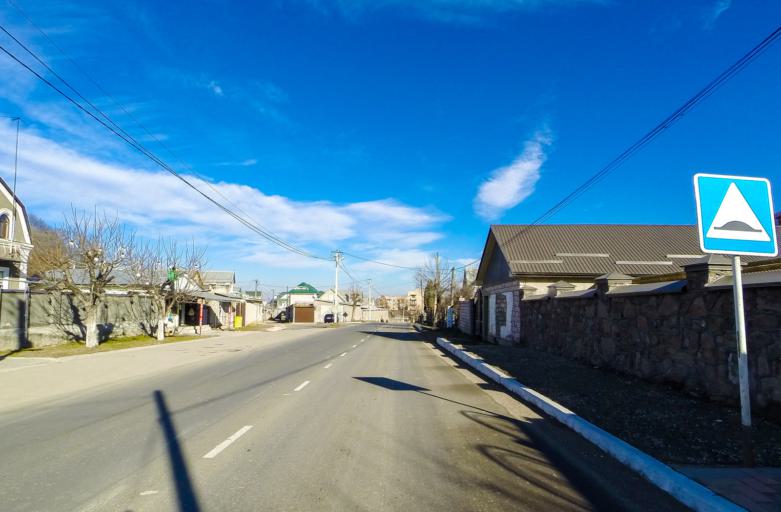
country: RU
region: Kabardino-Balkariya
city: Belaya Rechka
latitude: 43.4432
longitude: 43.5836
